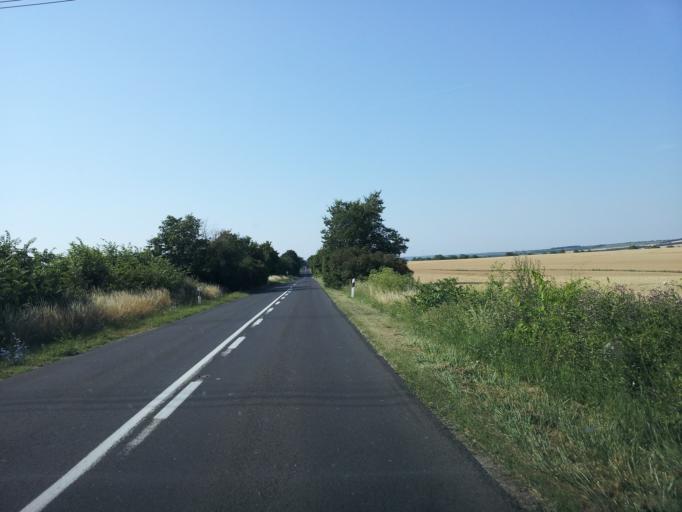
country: HU
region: Fejer
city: Lovasbereny
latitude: 47.3959
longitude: 18.5862
